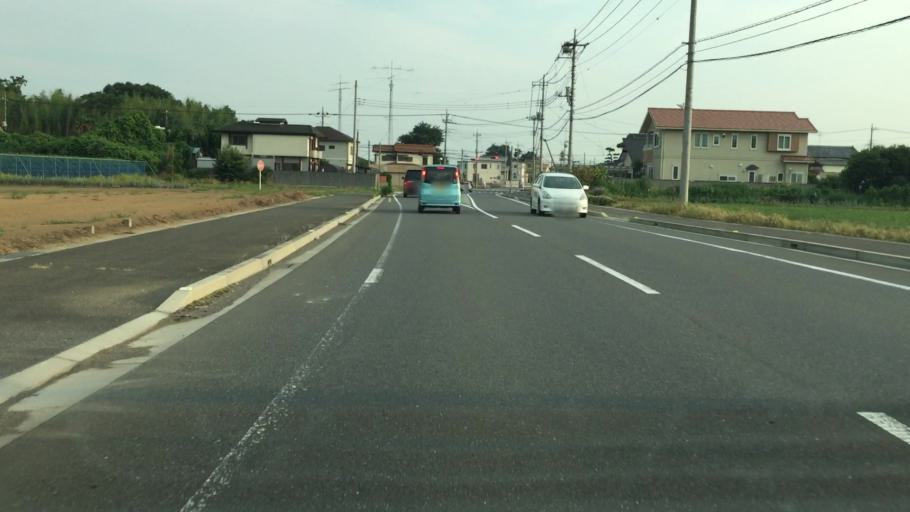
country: JP
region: Gunma
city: Tatebayashi
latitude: 36.2257
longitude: 139.5882
